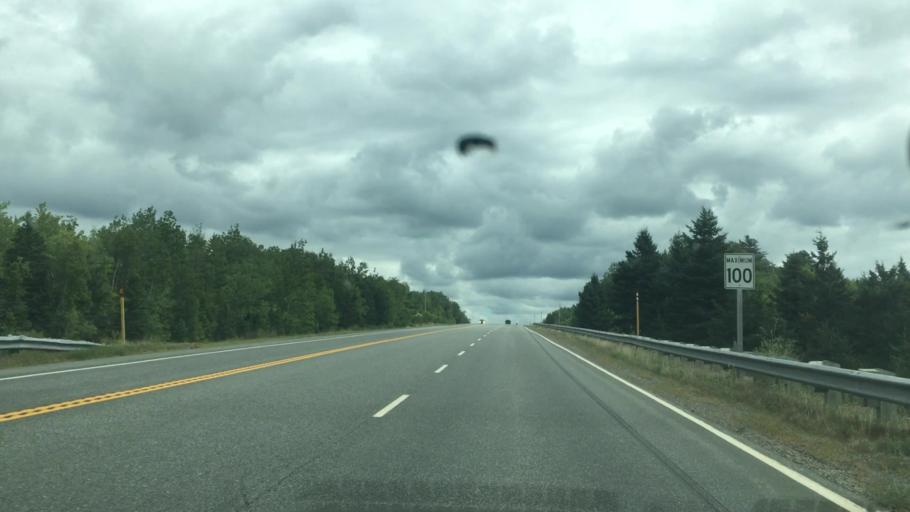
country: CA
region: Nova Scotia
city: New Glasgow
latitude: 45.5822
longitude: -62.3442
